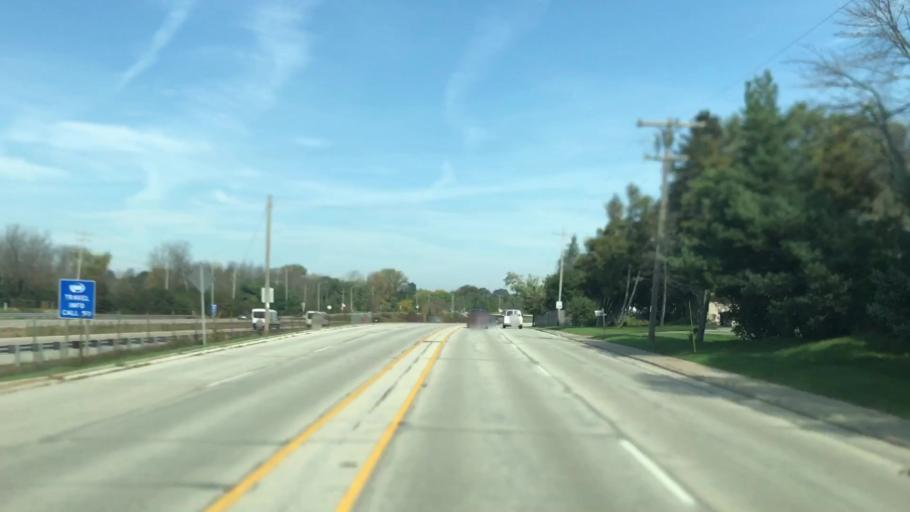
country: US
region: Wisconsin
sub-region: Milwaukee County
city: River Hills
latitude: 43.1884
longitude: -87.9228
